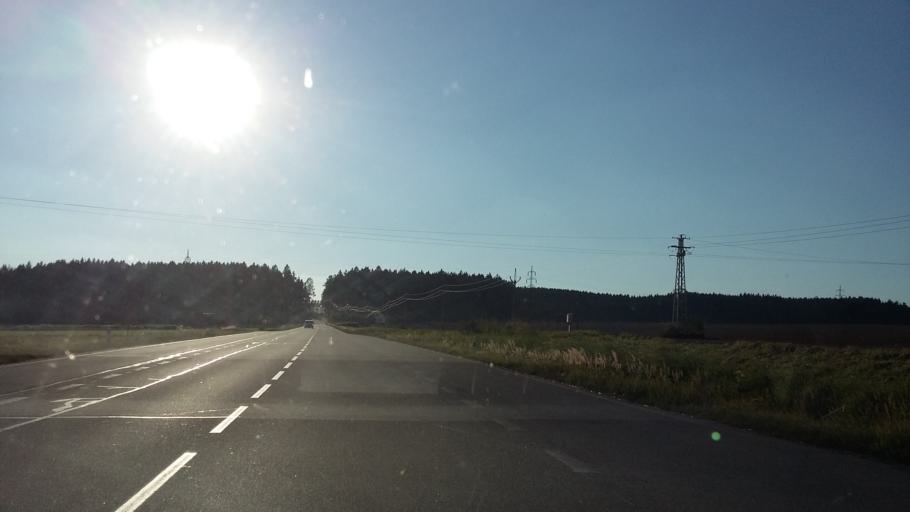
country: CZ
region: Vysocina
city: Luka nad Jihlavou
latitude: 49.3983
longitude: 15.7014
